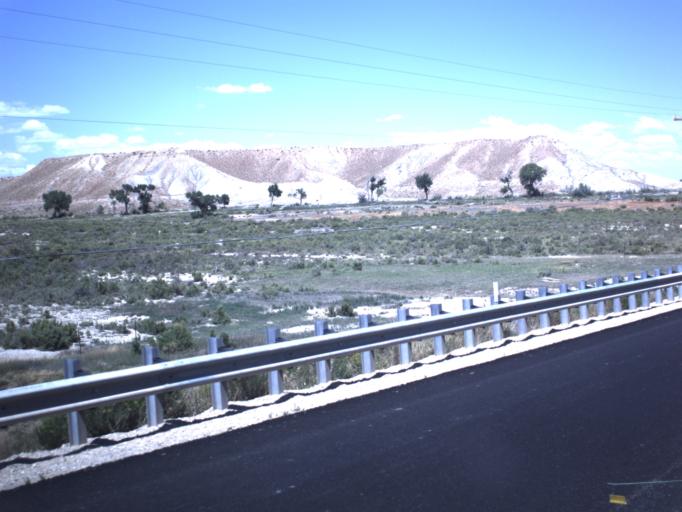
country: US
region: Utah
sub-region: Emery County
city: Castle Dale
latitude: 39.2320
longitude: -111.0144
